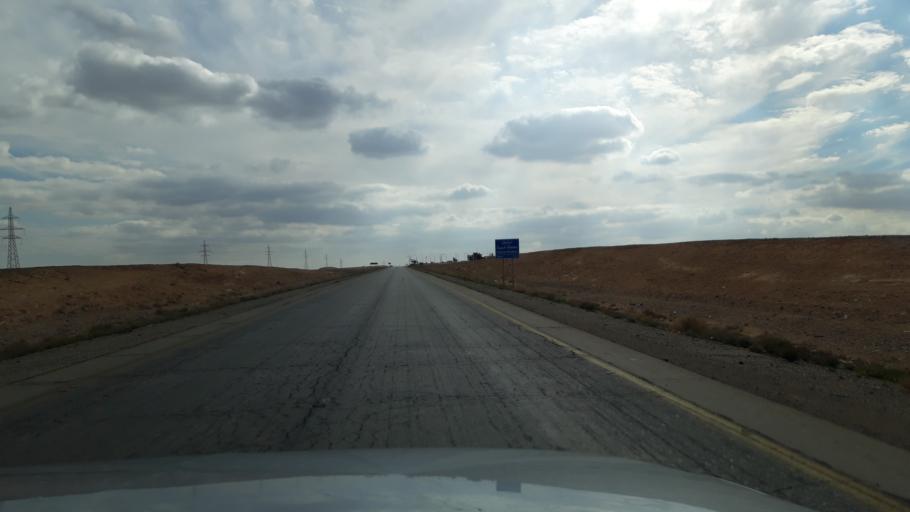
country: JO
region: Amman
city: Al Azraq ash Shamali
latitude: 31.7556
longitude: 36.5474
